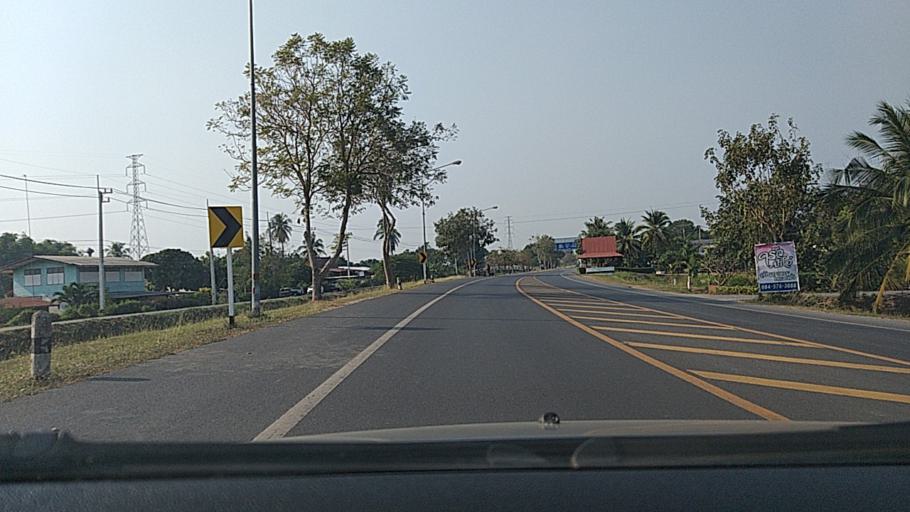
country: TH
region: Ang Thong
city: Chaiyo
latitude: 14.7164
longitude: 100.4338
